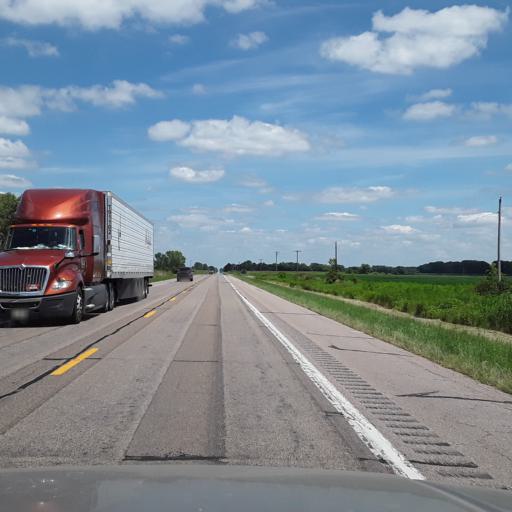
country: US
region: Nebraska
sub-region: Polk County
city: Osceola
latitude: 41.3565
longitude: -97.5678
